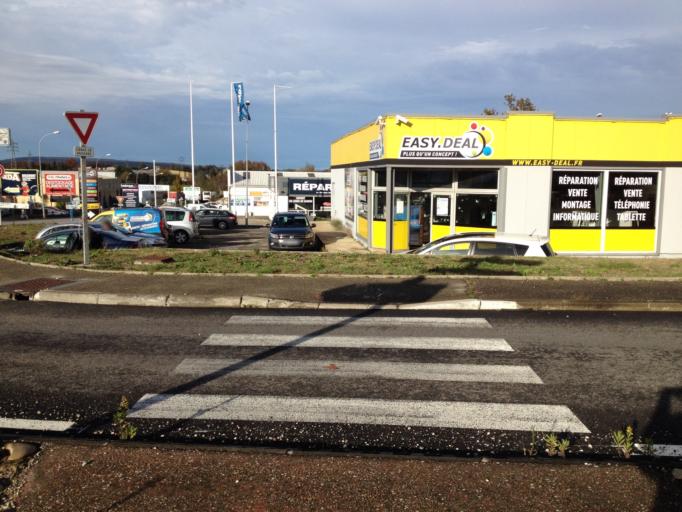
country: FR
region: Provence-Alpes-Cote d'Azur
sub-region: Departement du Vaucluse
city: Orange
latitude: 44.1215
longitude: 4.8407
